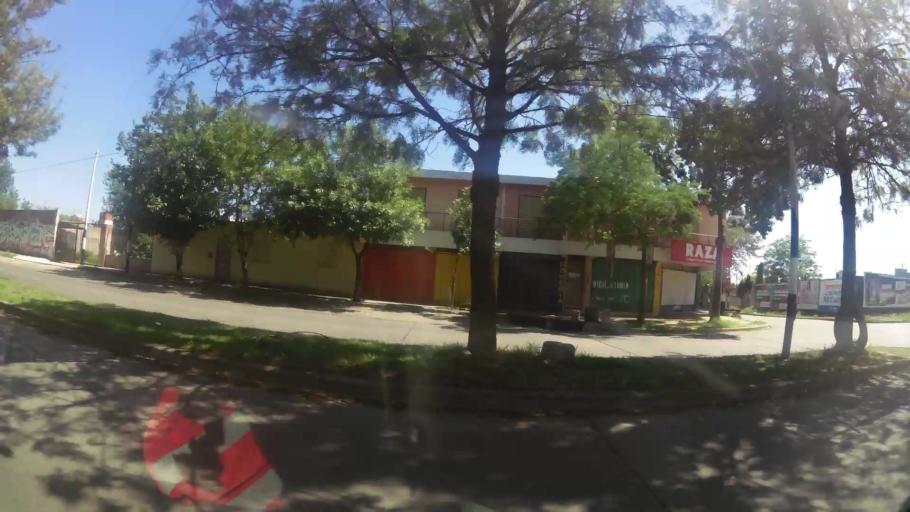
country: AR
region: Cordoba
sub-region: Departamento de Capital
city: Cordoba
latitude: -31.4198
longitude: -64.2185
